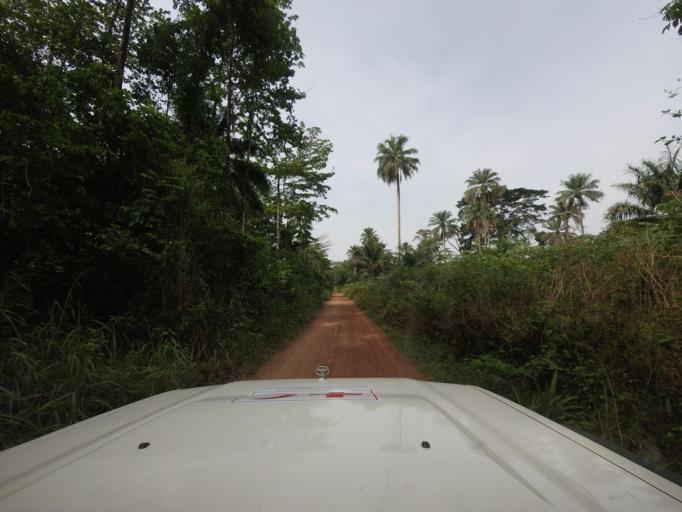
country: GN
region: Nzerekore
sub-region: Macenta
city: Macenta
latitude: 8.4902
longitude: -9.5384
